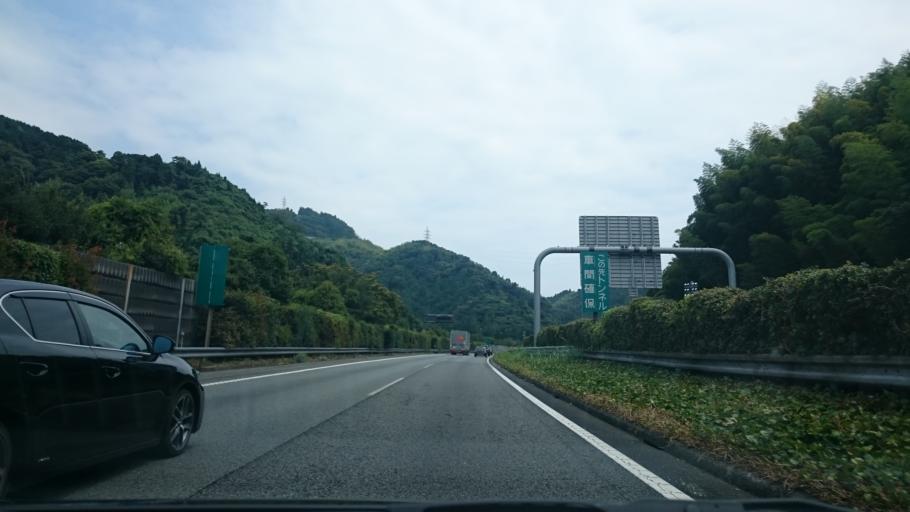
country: JP
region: Shizuoka
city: Fujinomiya
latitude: 35.0675
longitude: 138.5304
